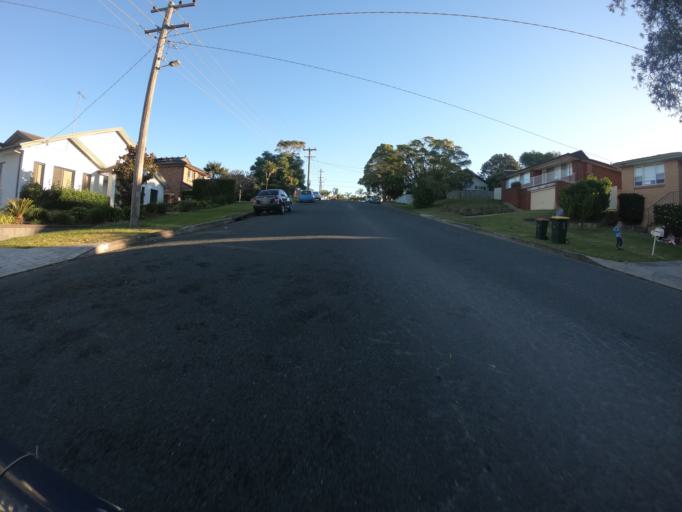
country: AU
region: New South Wales
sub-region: Wollongong
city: Cordeaux Heights
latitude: -34.4294
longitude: 150.8442
